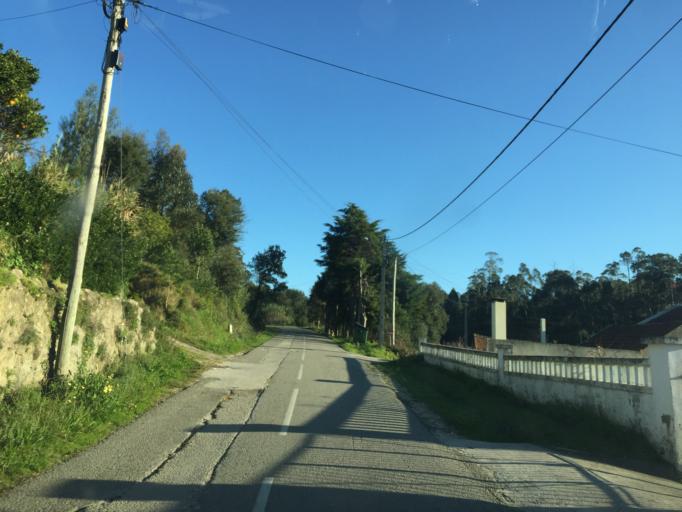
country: PT
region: Coimbra
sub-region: Figueira da Foz
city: Alhadas
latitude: 40.1631
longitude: -8.8089
